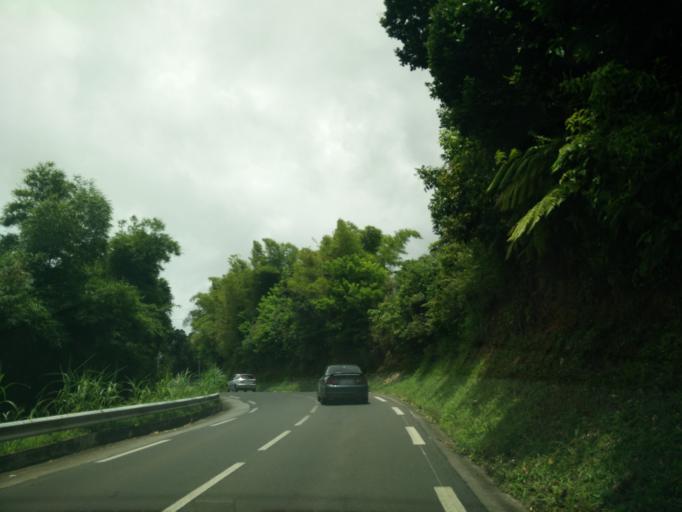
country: MQ
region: Martinique
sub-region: Martinique
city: Le Morne-Rouge
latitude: 14.7702
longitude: -61.1432
